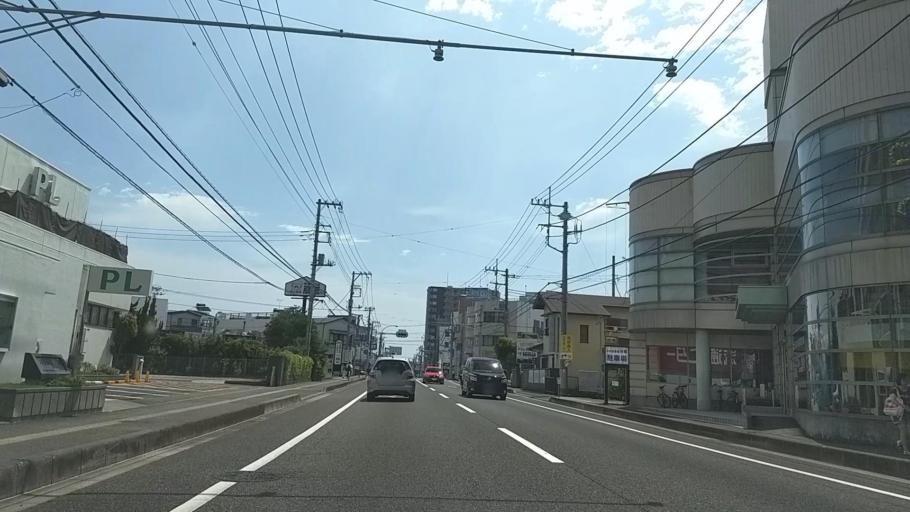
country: JP
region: Shizuoka
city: Fuji
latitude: 35.1629
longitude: 138.6790
